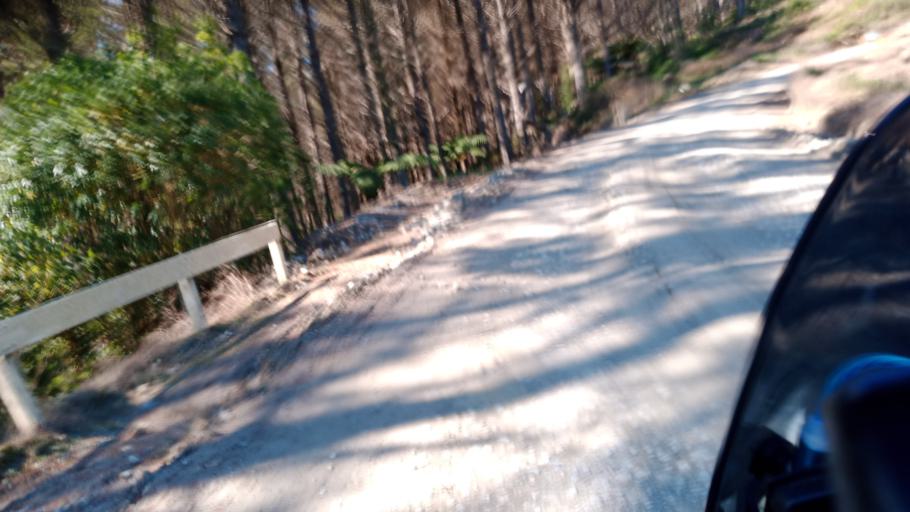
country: NZ
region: Gisborne
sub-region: Gisborne District
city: Gisborne
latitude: -38.8986
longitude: 177.8025
